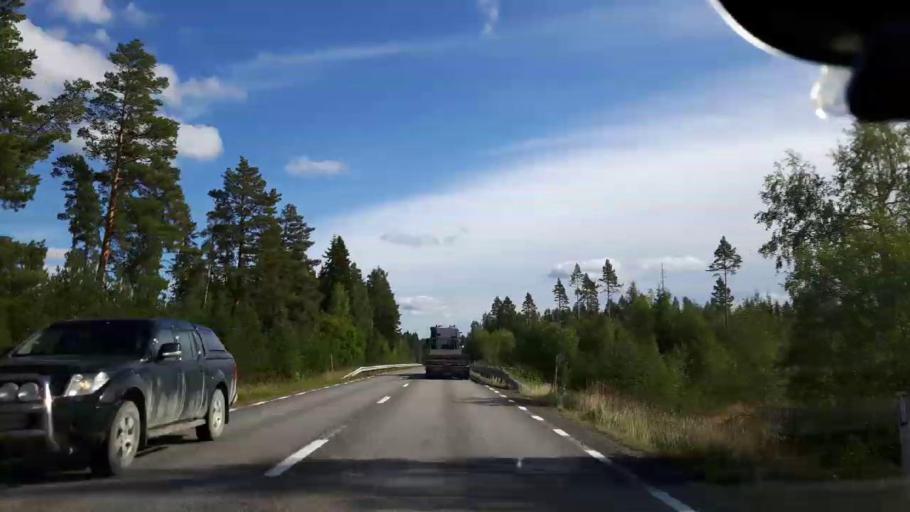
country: SE
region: Jaemtland
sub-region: Braecke Kommun
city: Braecke
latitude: 63.1934
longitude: 15.3853
